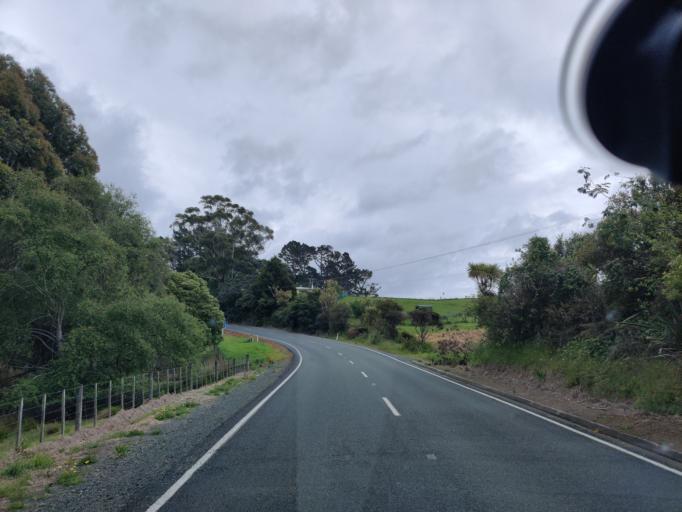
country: NZ
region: Auckland
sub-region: Auckland
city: Warkworth
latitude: -36.2822
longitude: 174.7930
